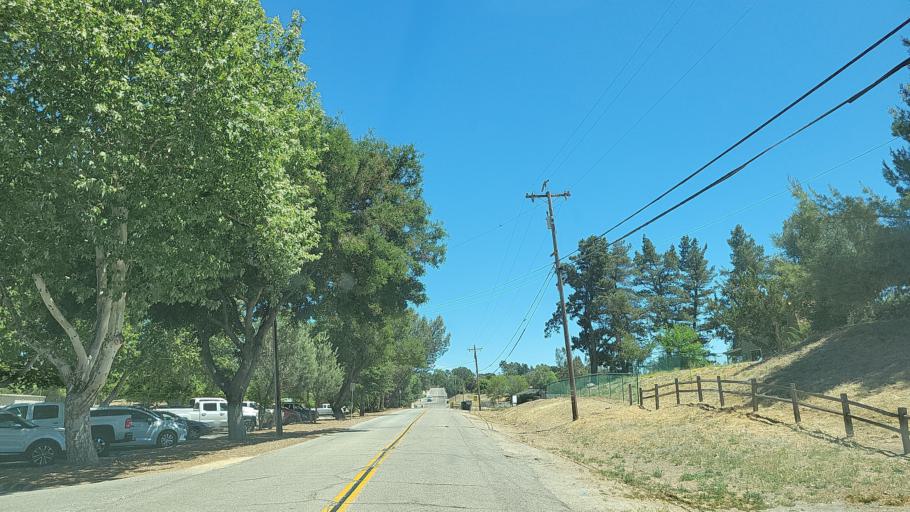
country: US
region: California
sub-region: San Luis Obispo County
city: Atascadero
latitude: 35.4531
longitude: -120.6352
